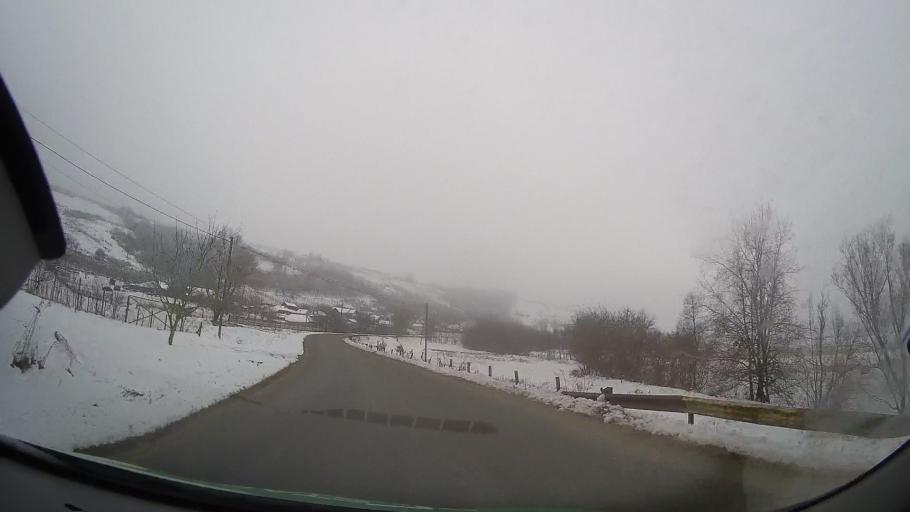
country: RO
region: Bacau
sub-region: Comuna Vultureni
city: Vultureni
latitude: 46.3935
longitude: 27.2780
